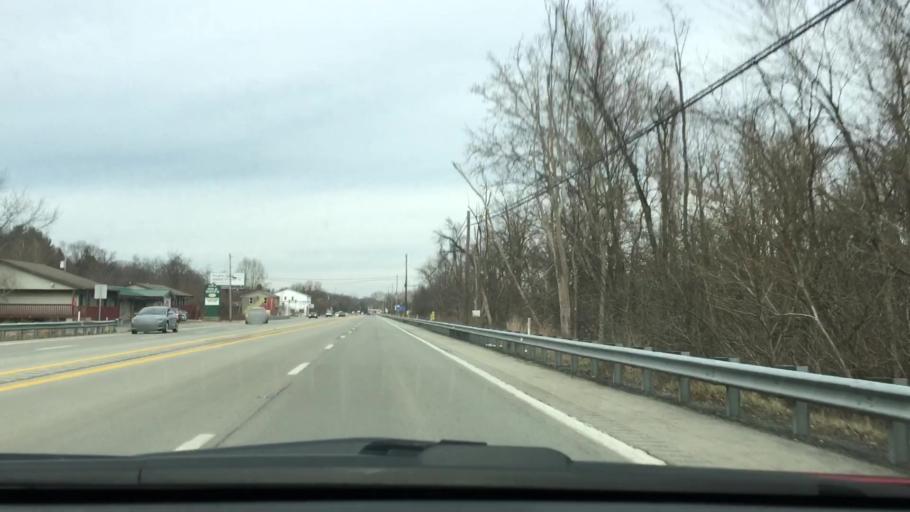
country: US
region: Pennsylvania
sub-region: Fayette County
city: Perryopolis
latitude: 40.0726
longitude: -79.7614
